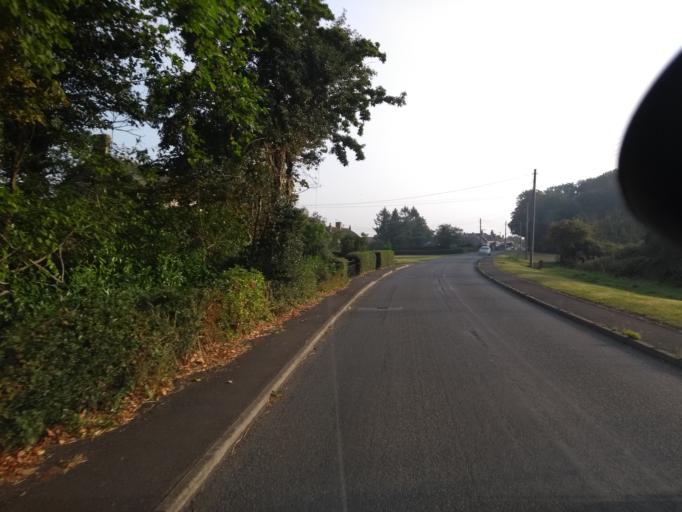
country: GB
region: England
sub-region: Somerset
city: Curry Rivel
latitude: 50.9898
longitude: -2.8638
